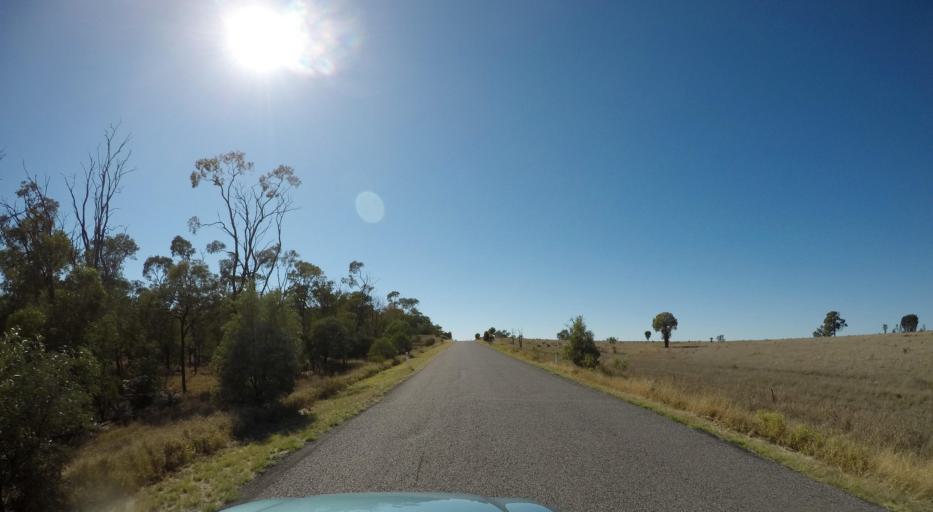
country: AU
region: Queensland
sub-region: Banana
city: Taroom
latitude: -25.7886
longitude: 149.6862
